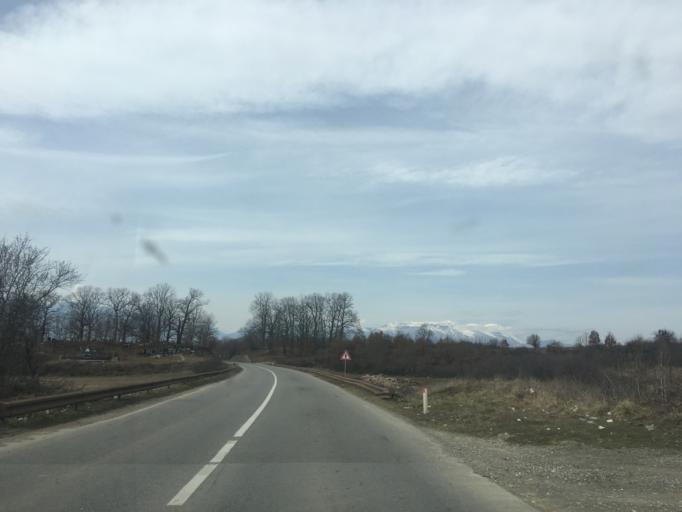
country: XK
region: Pec
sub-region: Komuna e Pejes
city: Kosuriq
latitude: 42.6198
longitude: 20.4861
